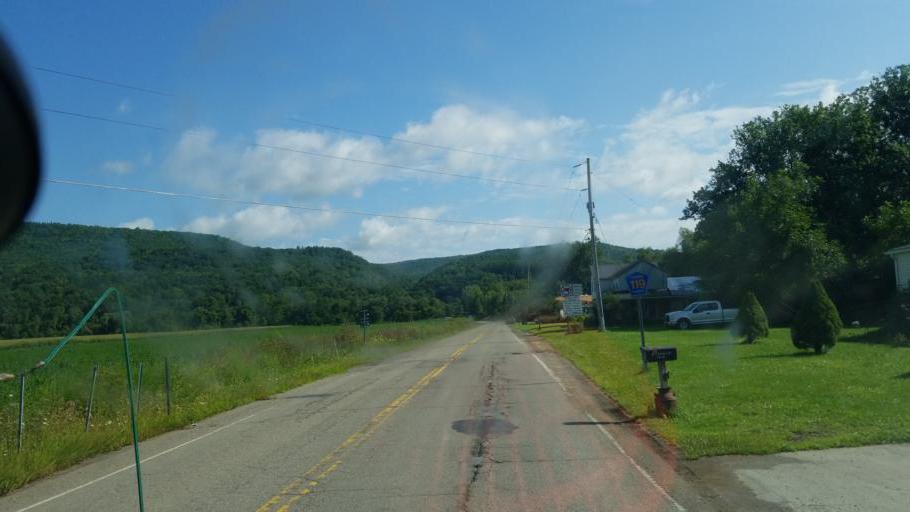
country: US
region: New York
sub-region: Steuben County
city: Canisteo
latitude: 42.2590
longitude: -77.5839
